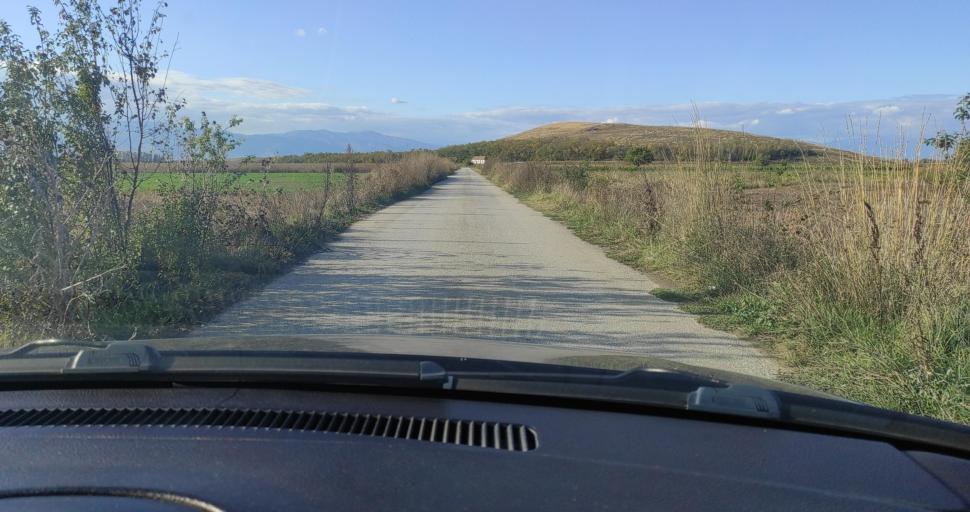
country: MK
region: Prilep
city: Topolcani
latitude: 41.2815
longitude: 21.4231
